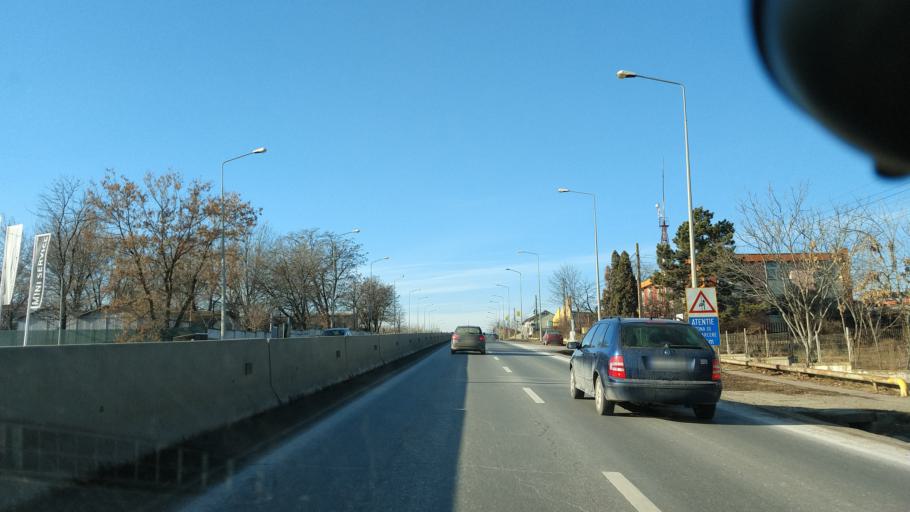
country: RO
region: Iasi
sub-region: Comuna Valea Lupului
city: Valea Lupului
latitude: 47.1761
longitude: 27.4948
